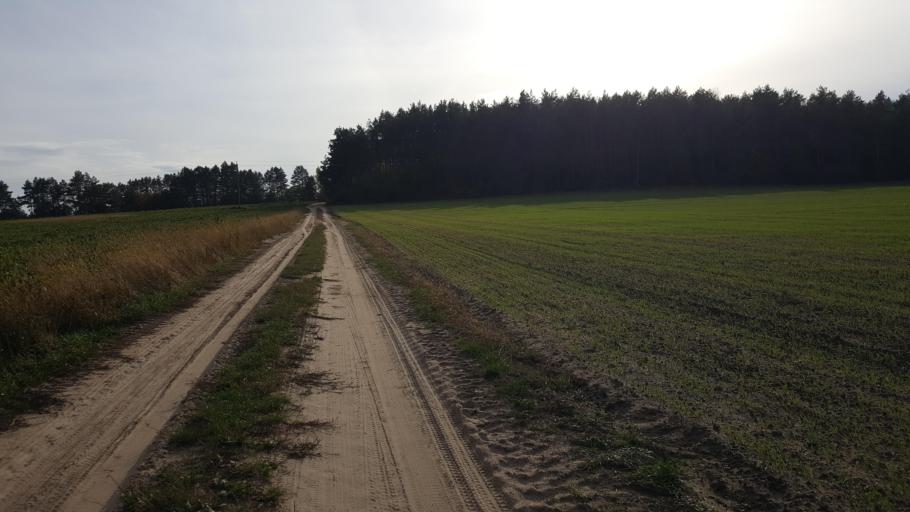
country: BY
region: Brest
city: Kamyanyets
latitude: 52.3897
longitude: 23.8487
